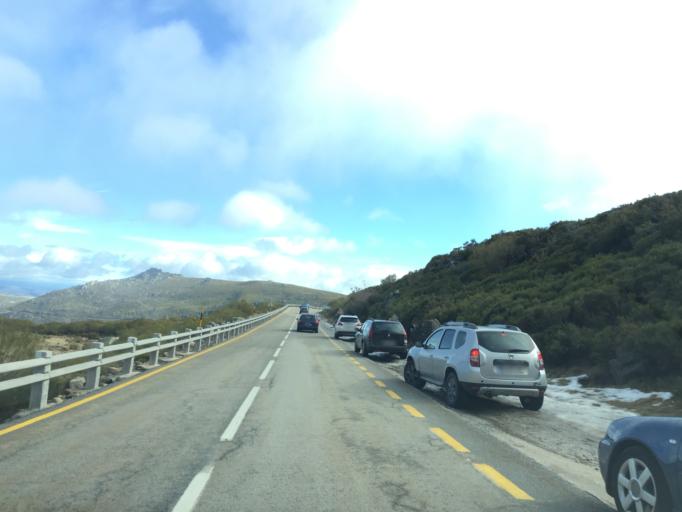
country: PT
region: Castelo Branco
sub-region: Covilha
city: Covilha
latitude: 40.3226
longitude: -7.5904
